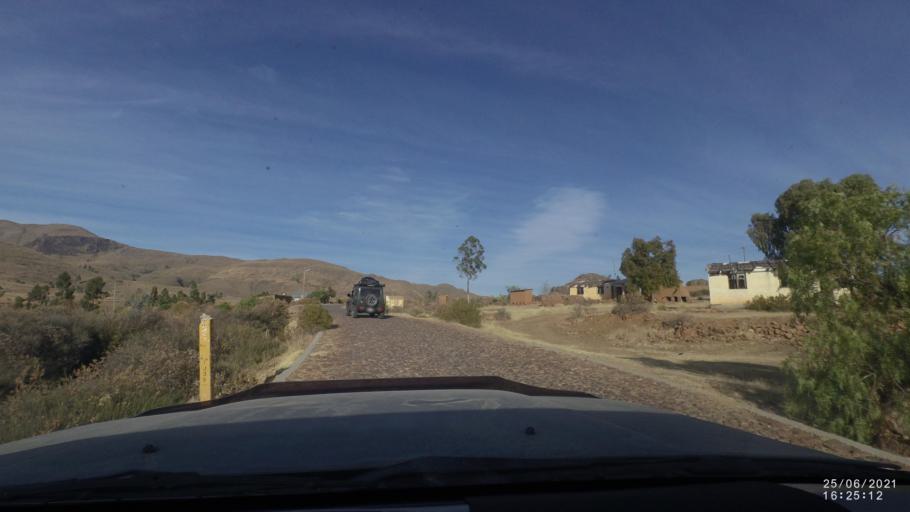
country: BO
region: Cochabamba
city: Arani
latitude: -17.7669
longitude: -65.8209
